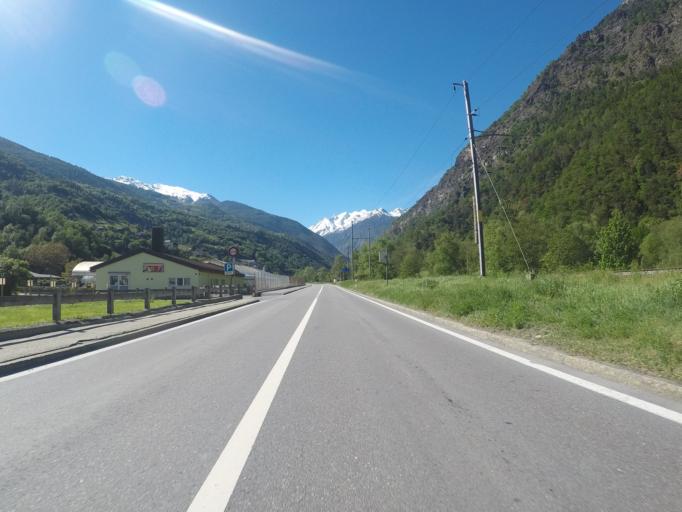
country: CH
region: Valais
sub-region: Visp District
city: Visp
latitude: 46.2859
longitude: 7.8806
